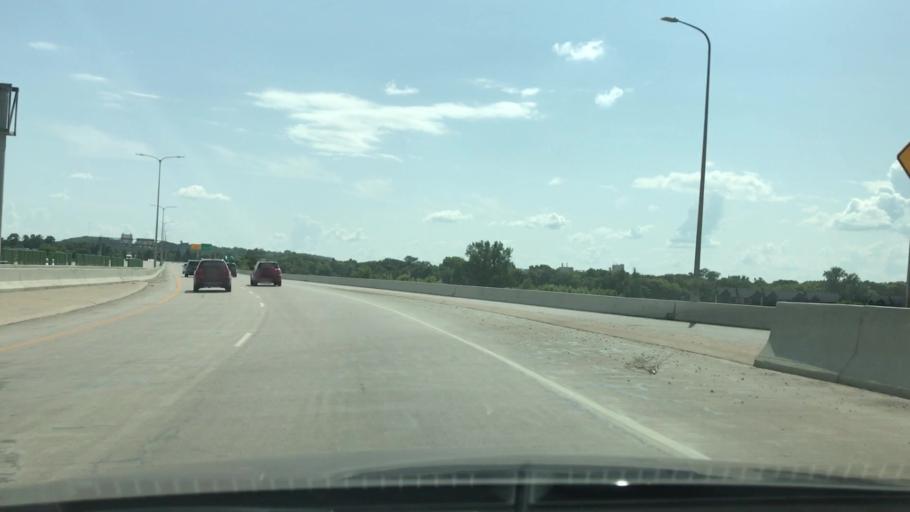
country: US
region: Minnesota
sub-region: Blue Earth County
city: Mankato
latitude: 44.1662
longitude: -94.0168
